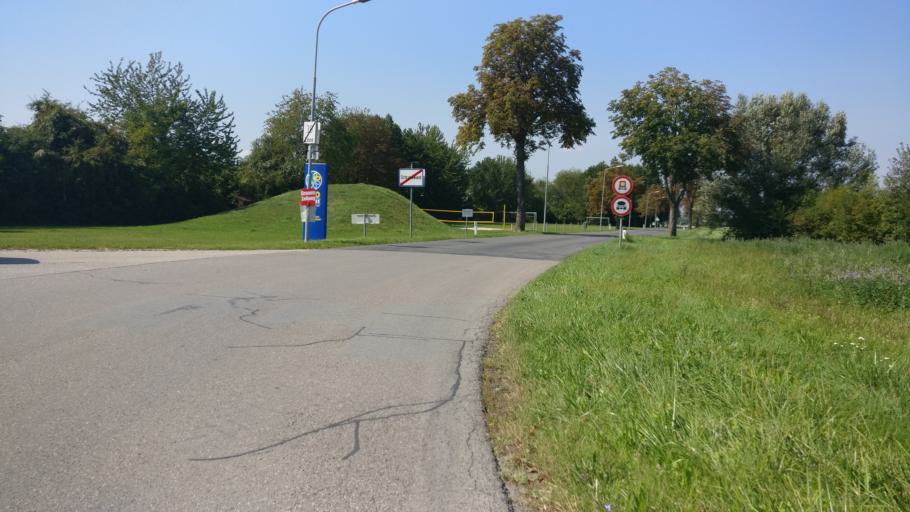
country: AT
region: Lower Austria
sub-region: Politischer Bezirk Baden
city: Mitterndorf an der Fischa
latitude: 47.9788
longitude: 16.4400
